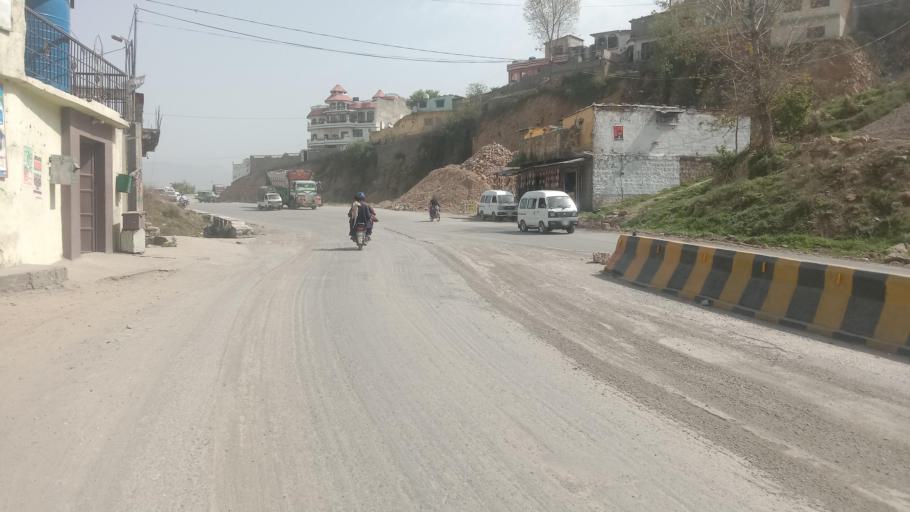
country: PK
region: Khyber Pakhtunkhwa
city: Abbottabad
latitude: 34.1252
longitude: 73.1911
